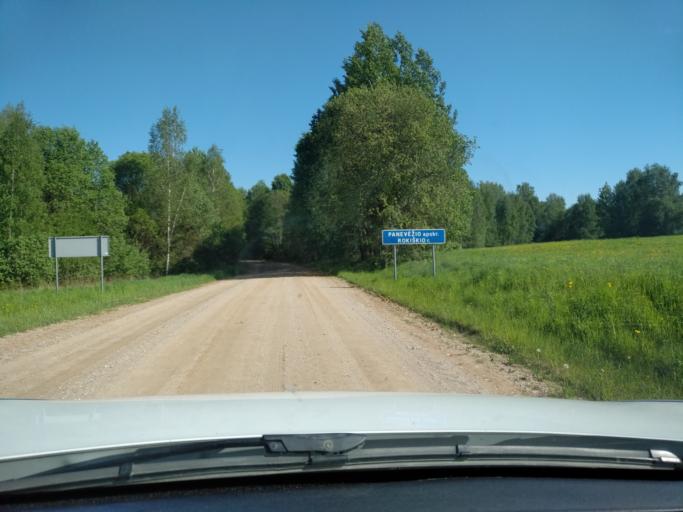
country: LT
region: Utenos apskritis
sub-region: Utena
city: Utena
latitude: 55.7192
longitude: 25.5362
